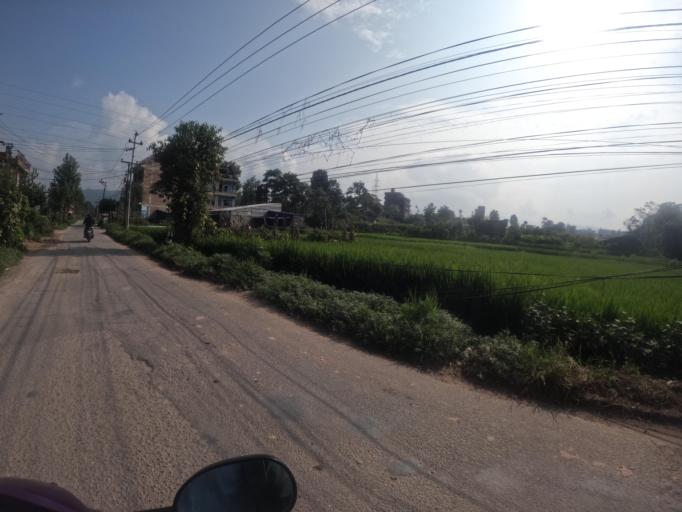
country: NP
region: Central Region
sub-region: Bagmati Zone
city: Bhaktapur
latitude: 27.6824
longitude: 85.4367
